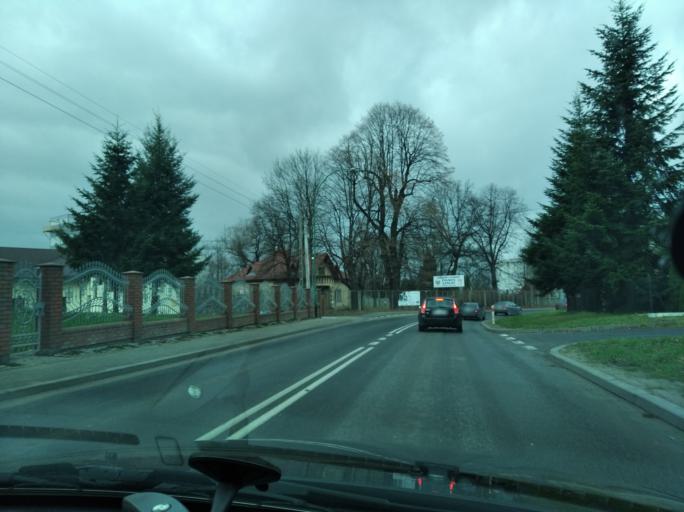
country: PL
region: Subcarpathian Voivodeship
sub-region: Powiat lancucki
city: Lancut
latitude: 50.0796
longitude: 22.2329
